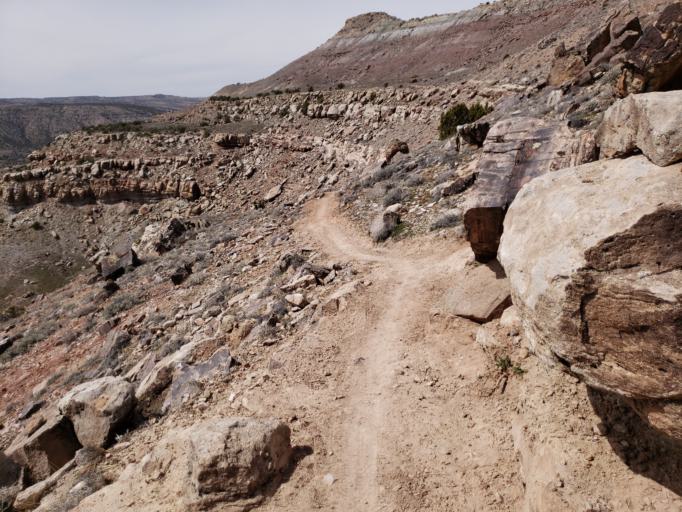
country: US
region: Colorado
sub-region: Mesa County
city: Loma
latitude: 39.1841
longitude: -108.8555
